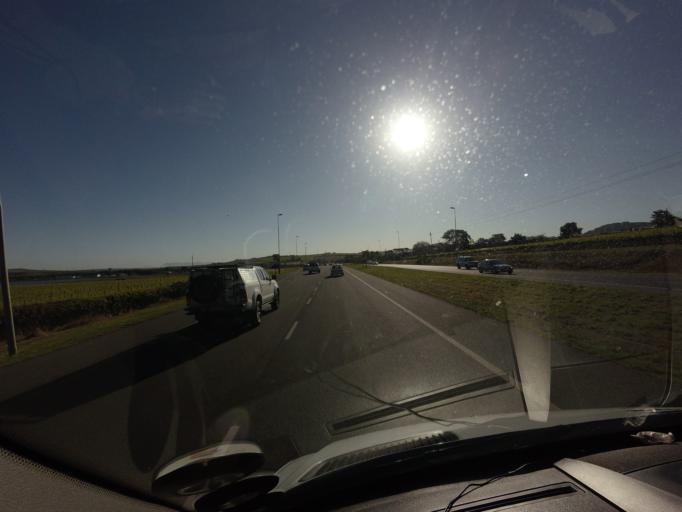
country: ZA
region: Western Cape
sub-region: Cape Winelands District Municipality
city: Stellenbosch
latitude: -33.9500
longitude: 18.8120
